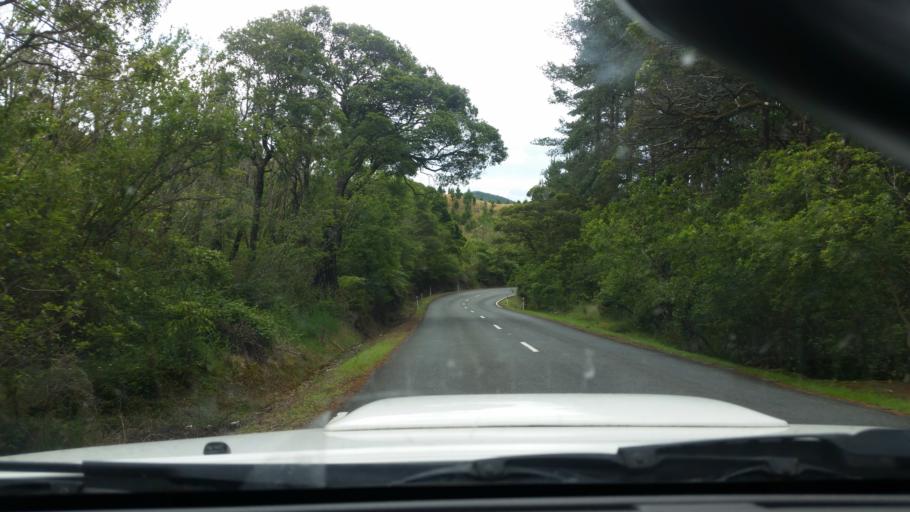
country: NZ
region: Northland
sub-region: Kaipara District
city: Dargaville
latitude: -35.7262
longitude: 173.8606
